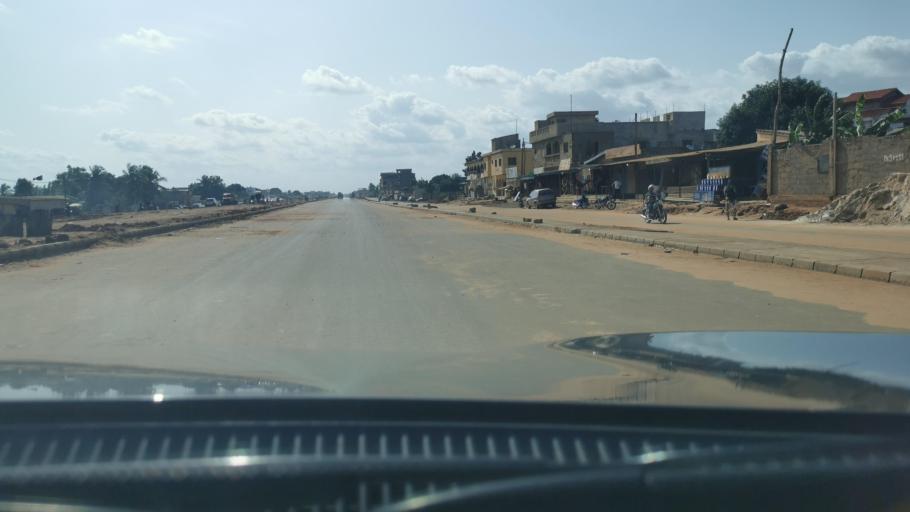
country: TG
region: Maritime
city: Lome
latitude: 6.2078
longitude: 1.1404
